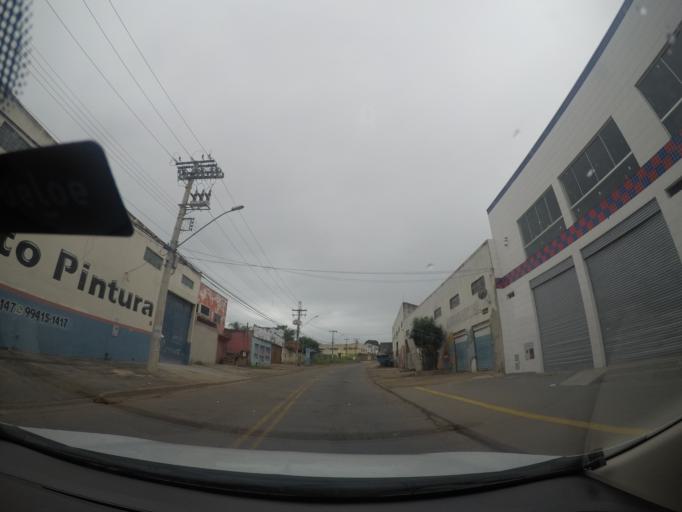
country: BR
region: Goias
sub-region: Goiania
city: Goiania
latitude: -16.6554
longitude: -49.3165
